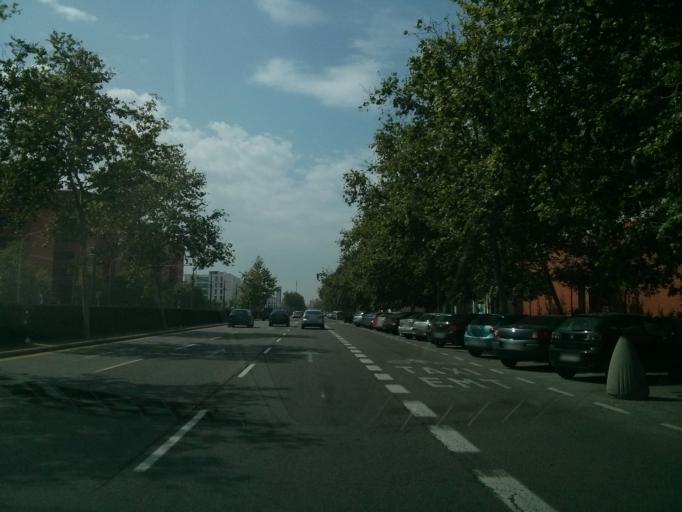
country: ES
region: Valencia
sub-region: Provincia de Valencia
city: Alboraya
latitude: 39.4788
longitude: -0.3410
